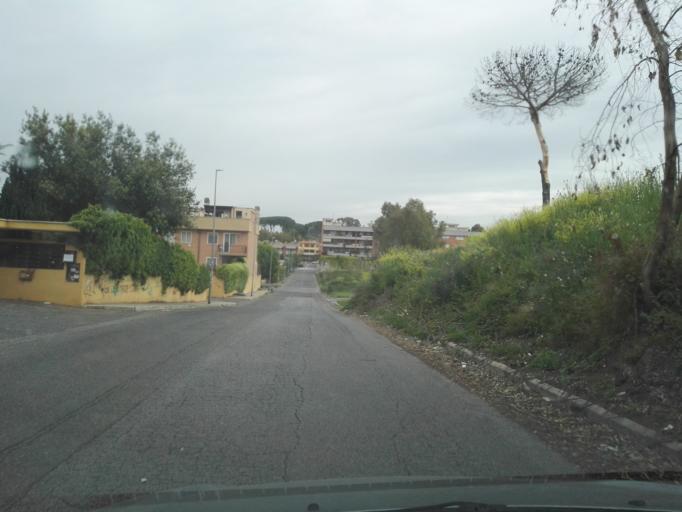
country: IT
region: Latium
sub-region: Citta metropolitana di Roma Capitale
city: Selcetta
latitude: 41.7692
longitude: 12.4766
